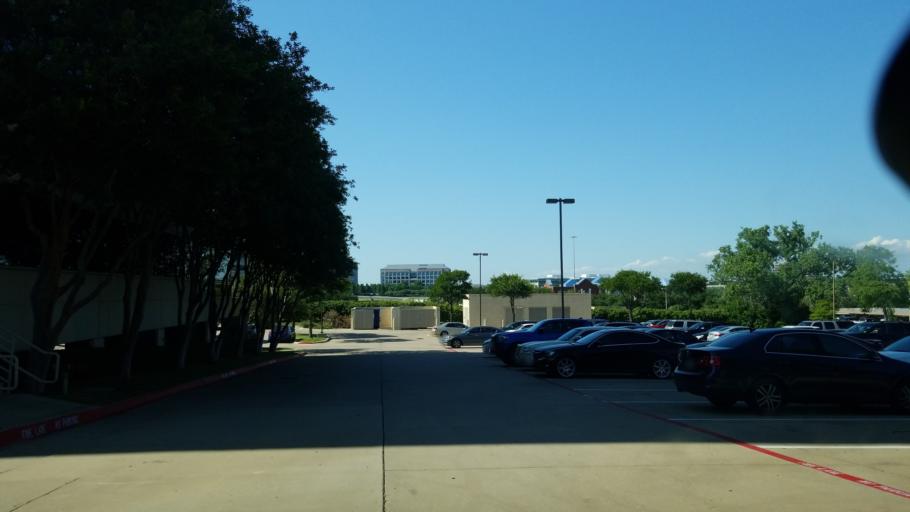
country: US
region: Texas
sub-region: Dallas County
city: Irving
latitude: 32.8878
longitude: -96.9675
